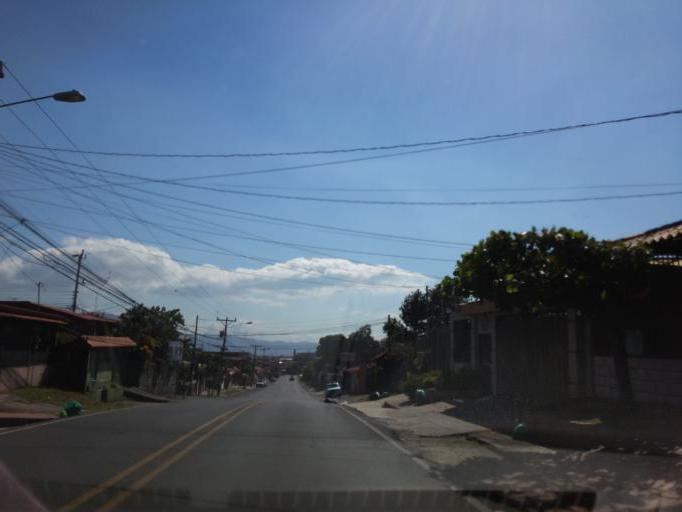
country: CR
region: Alajuela
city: Alajuela
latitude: 10.0287
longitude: -84.2052
